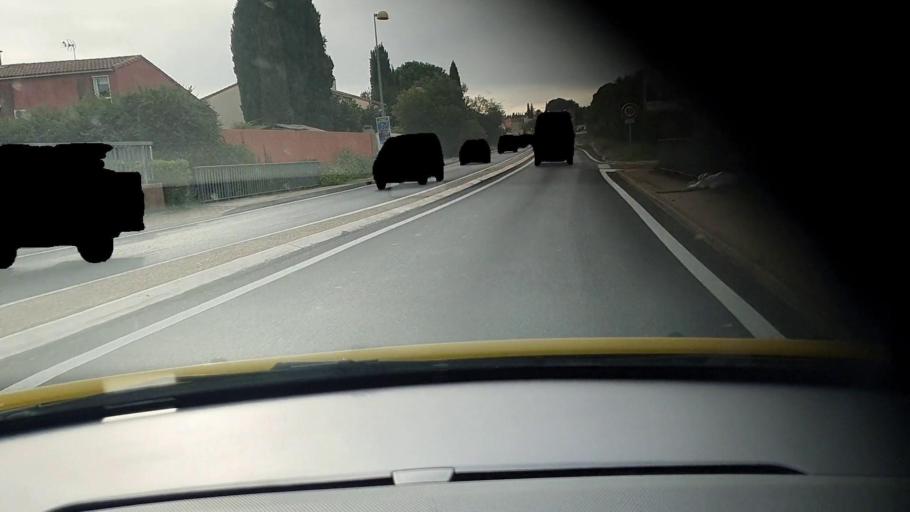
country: FR
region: Languedoc-Roussillon
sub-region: Departement du Gard
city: Caissargues
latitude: 43.7897
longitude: 4.3874
